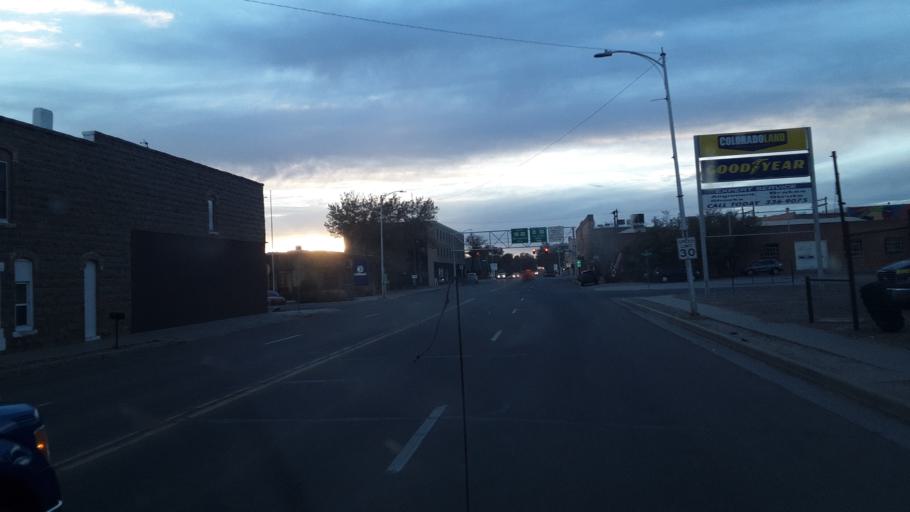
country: US
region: Colorado
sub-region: Prowers County
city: Lamar
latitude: 38.0884
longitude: -102.6172
